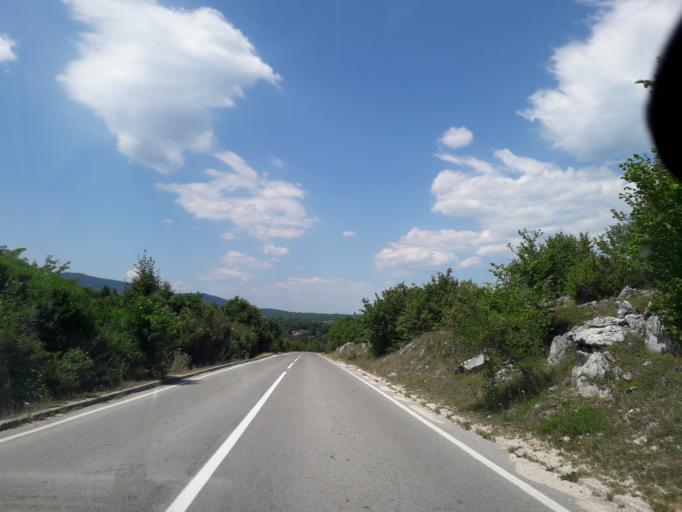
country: BA
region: Republika Srpska
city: Sipovo
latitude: 44.1435
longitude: 17.1772
